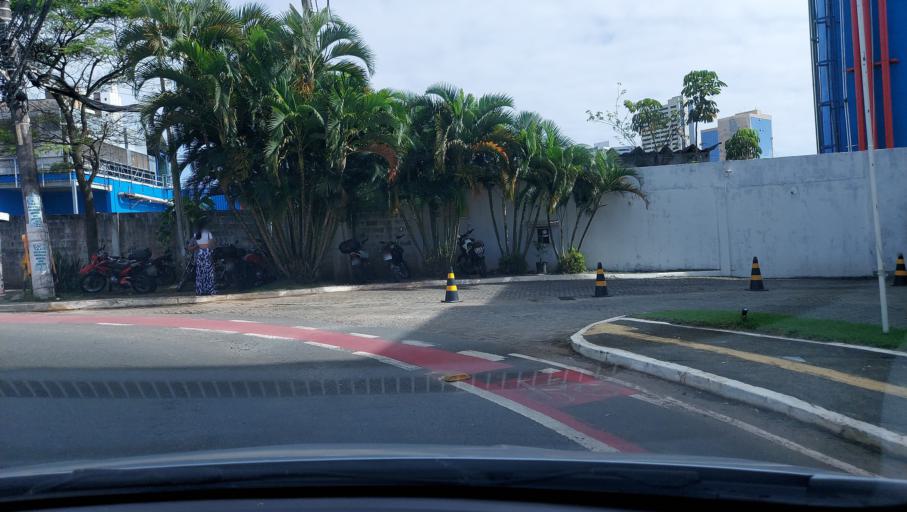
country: BR
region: Bahia
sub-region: Salvador
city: Salvador
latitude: -12.9840
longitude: -38.4647
